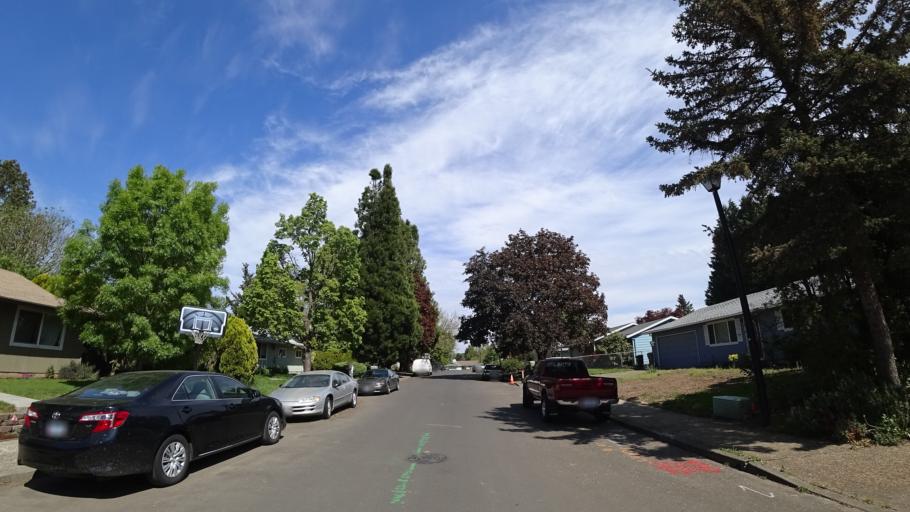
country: US
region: Oregon
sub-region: Washington County
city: Aloha
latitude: 45.4909
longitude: -122.8846
